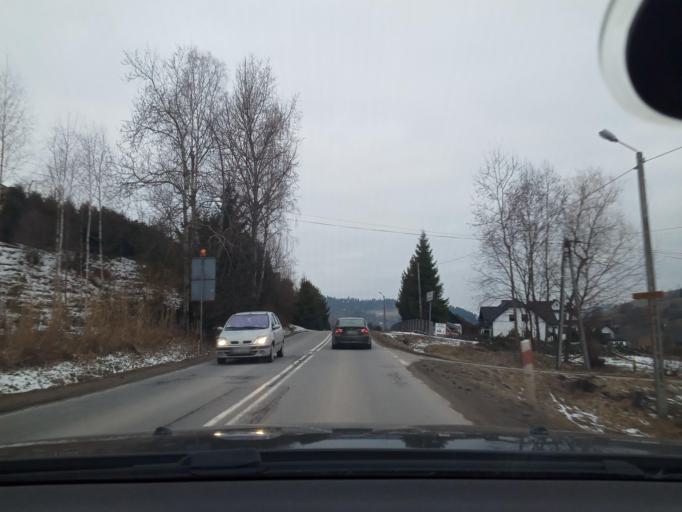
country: PL
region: Lesser Poland Voivodeship
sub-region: Powiat limanowski
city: Mszana Gorna
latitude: 49.6366
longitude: 20.1321
